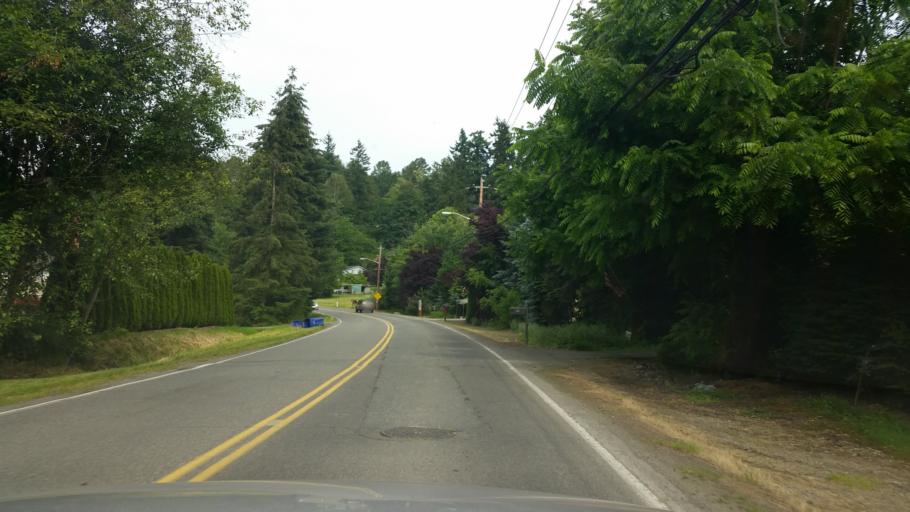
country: US
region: Washington
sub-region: King County
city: Bothell
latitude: 47.7526
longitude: -122.1917
